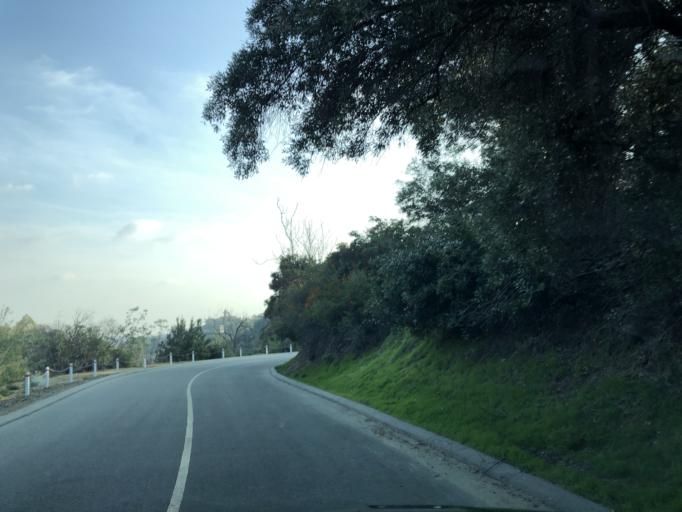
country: US
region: California
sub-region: Los Angeles County
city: Echo Park
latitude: 34.0822
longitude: -118.2323
